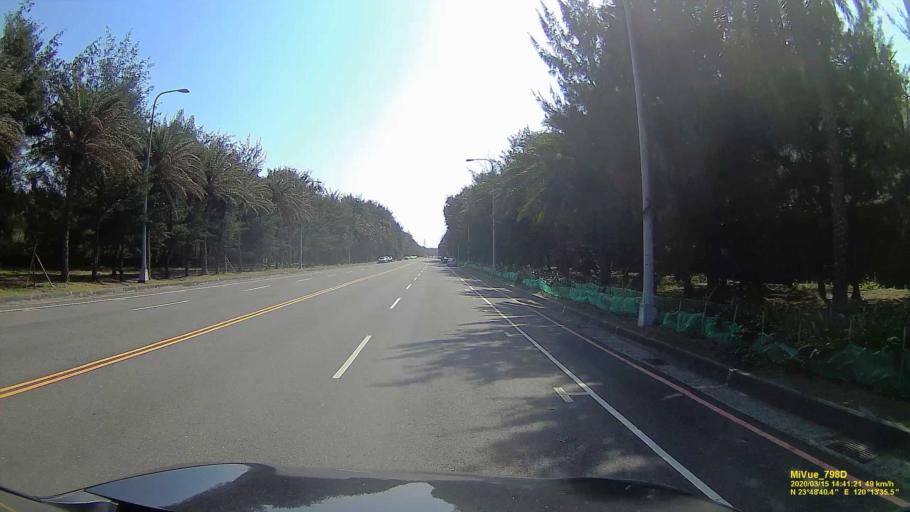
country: TW
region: Taiwan
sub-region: Yunlin
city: Douliu
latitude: 23.8110
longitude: 120.2264
